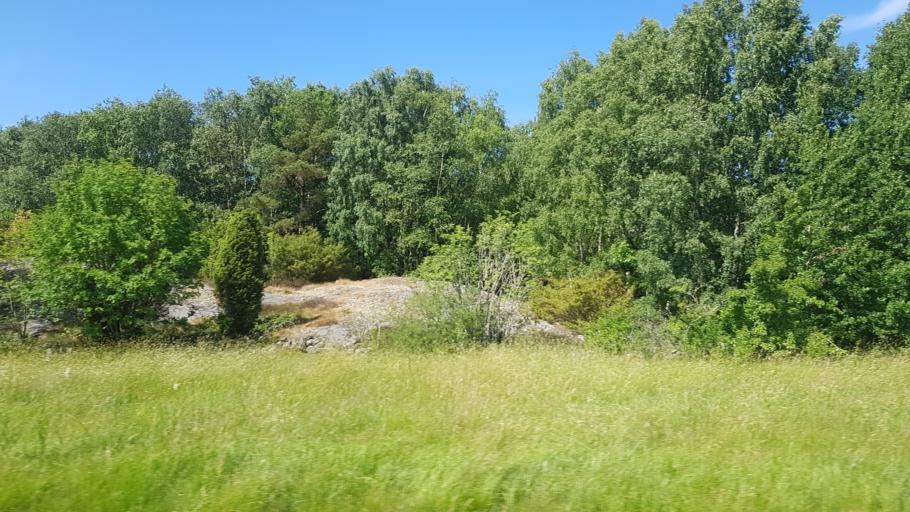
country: SE
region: Vaestra Goetaland
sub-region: Tjorns Kommun
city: Skaerhamn
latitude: 57.9863
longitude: 11.5700
